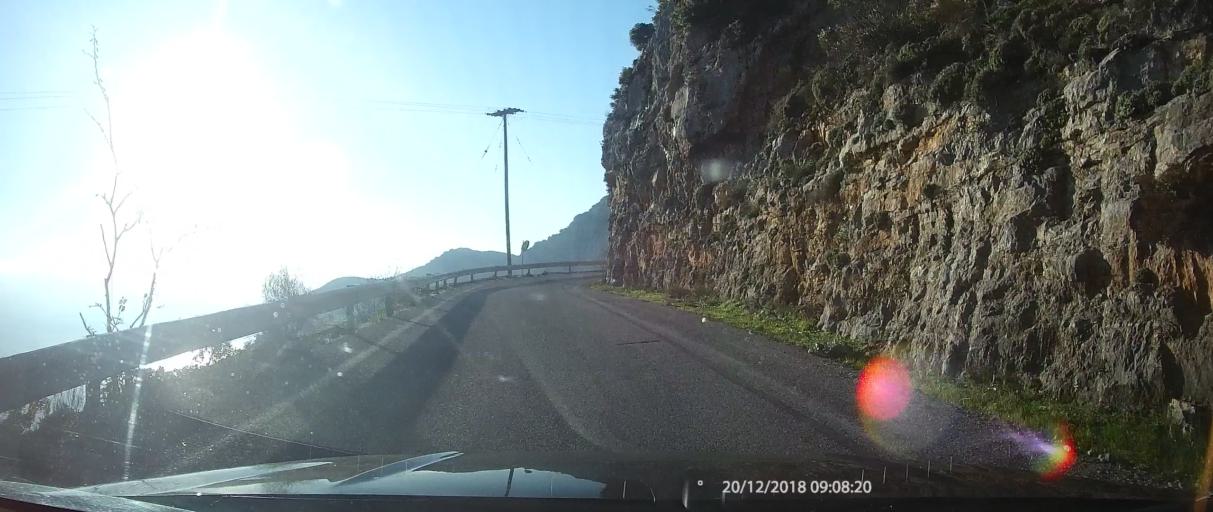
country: GR
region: Peloponnese
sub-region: Nomos Lakonias
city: Sykea
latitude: 36.9225
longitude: 23.0083
